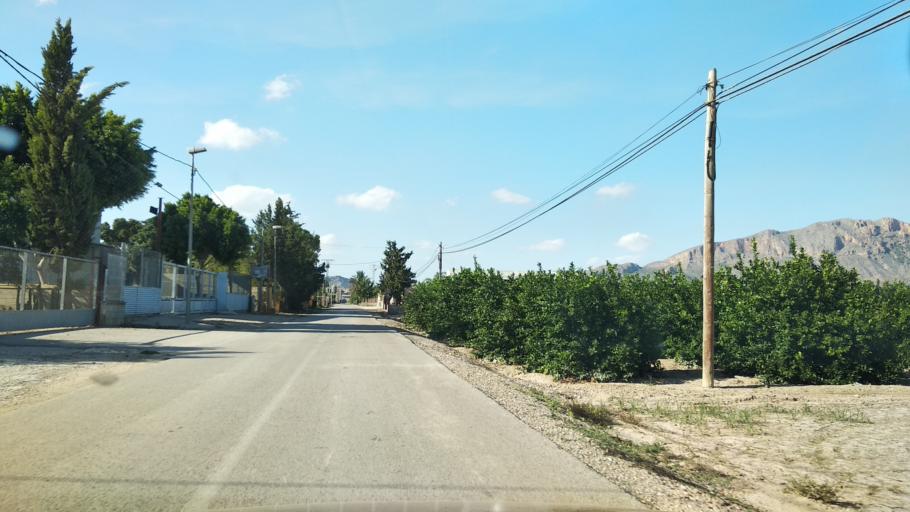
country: ES
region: Murcia
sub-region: Murcia
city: Santomera
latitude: 38.0514
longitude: -1.0407
